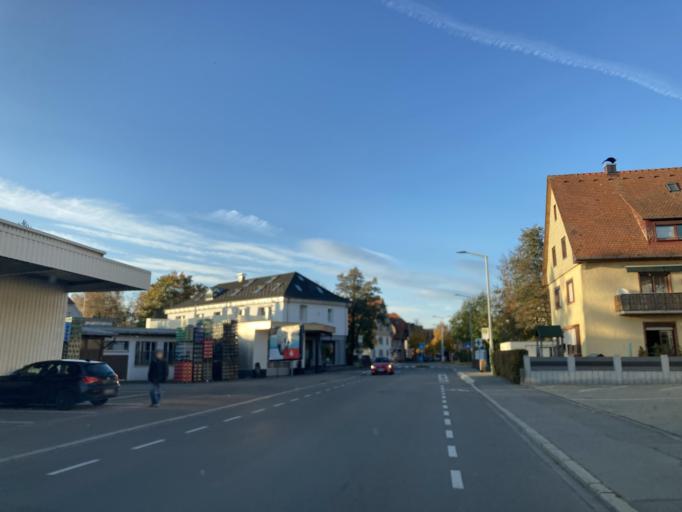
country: DE
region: Baden-Wuerttemberg
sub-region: Freiburg Region
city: Villingen-Schwenningen
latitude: 48.0502
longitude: 8.4617
